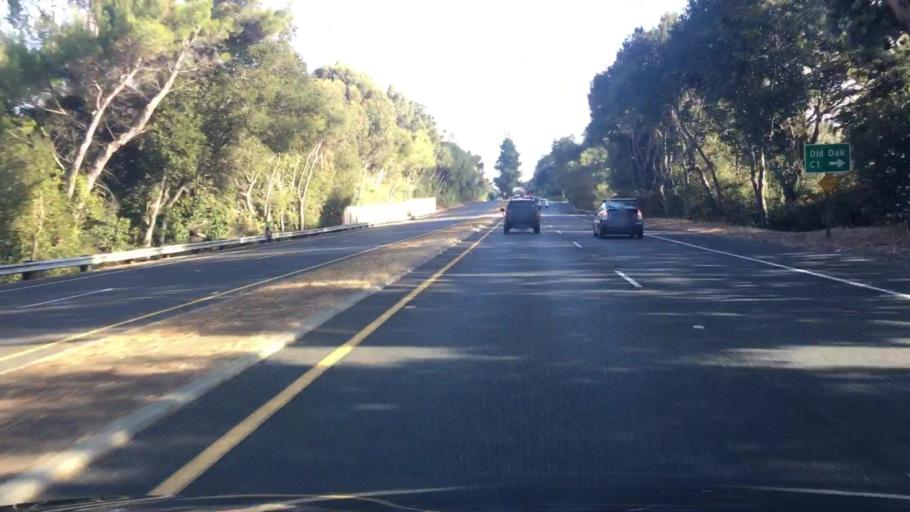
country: US
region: California
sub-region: Santa Clara County
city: Los Altos
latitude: 37.3860
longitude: -122.1250
